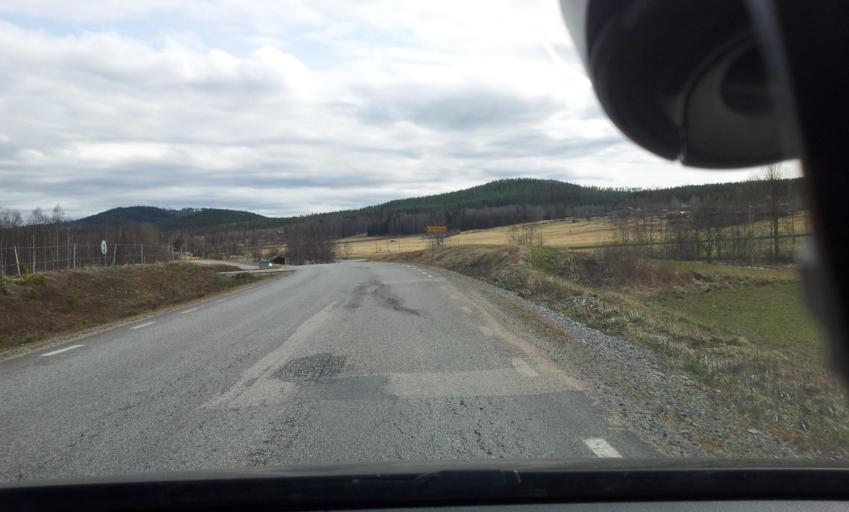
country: SE
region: Gaevleborg
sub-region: Ljusdals Kommun
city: Farila
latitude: 61.7740
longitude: 15.9574
